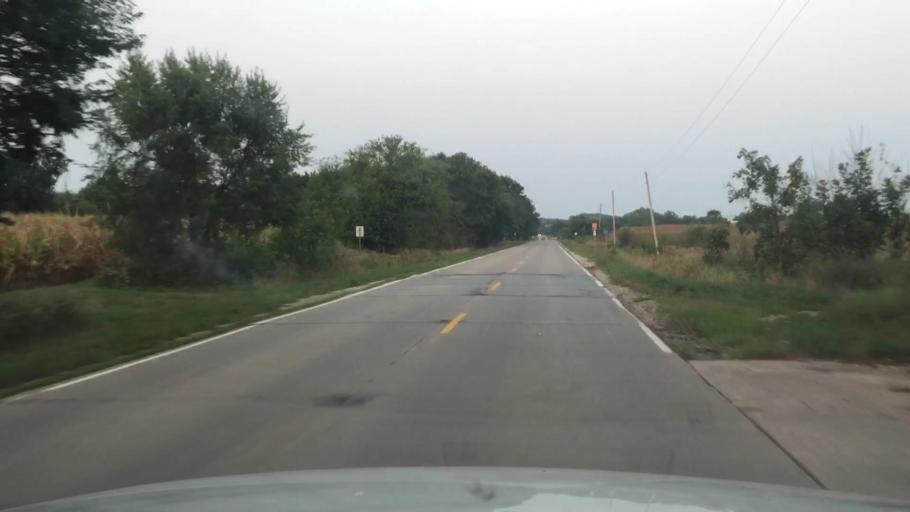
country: US
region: Iowa
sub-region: Clarke County
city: Osceola
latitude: 41.1802
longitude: -93.7254
